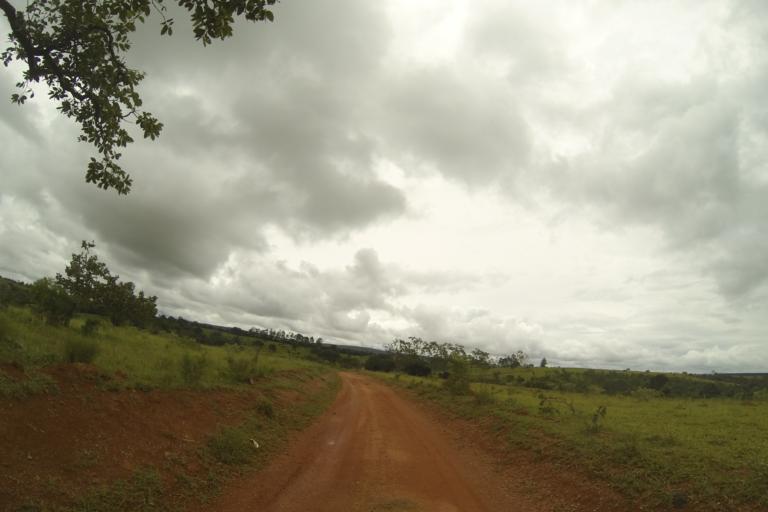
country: BR
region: Minas Gerais
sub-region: Ibia
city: Ibia
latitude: -19.7273
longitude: -46.5950
